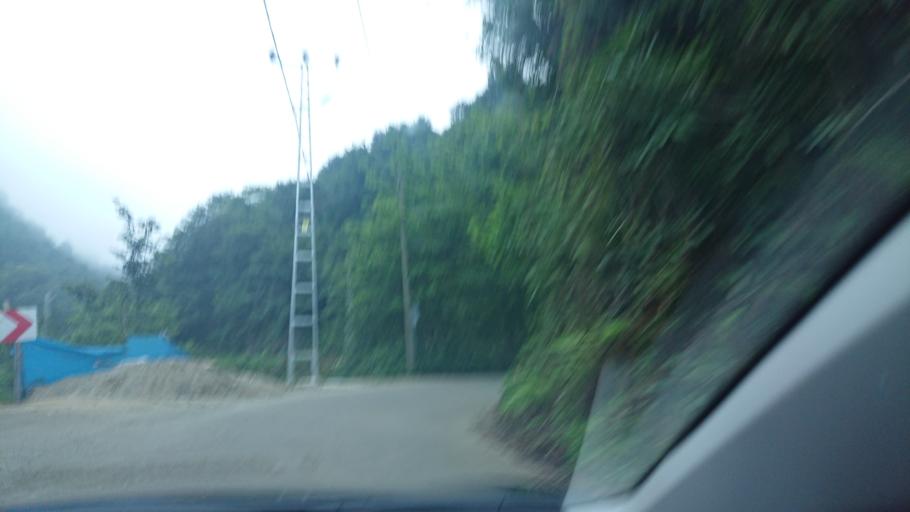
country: TR
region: Rize
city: Cayeli
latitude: 41.0481
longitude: 40.7984
